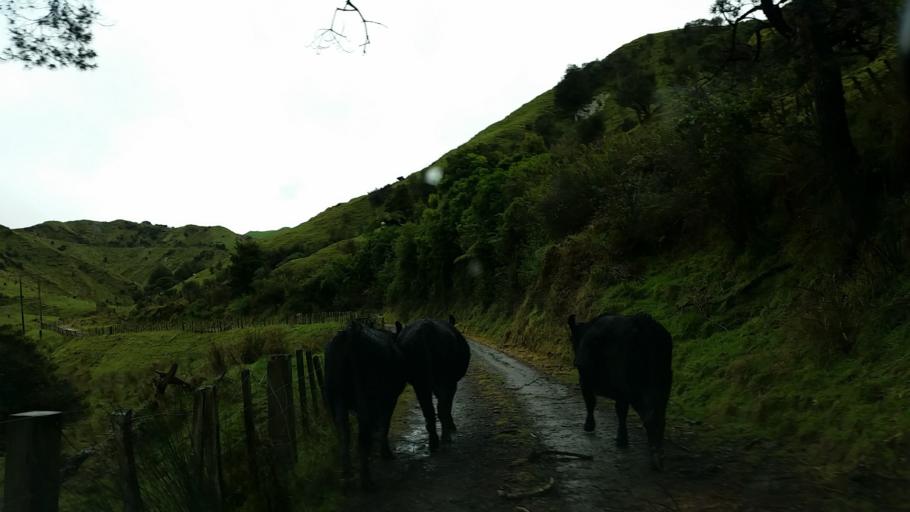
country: NZ
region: Taranaki
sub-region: South Taranaki District
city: Eltham
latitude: -39.4875
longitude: 174.4346
